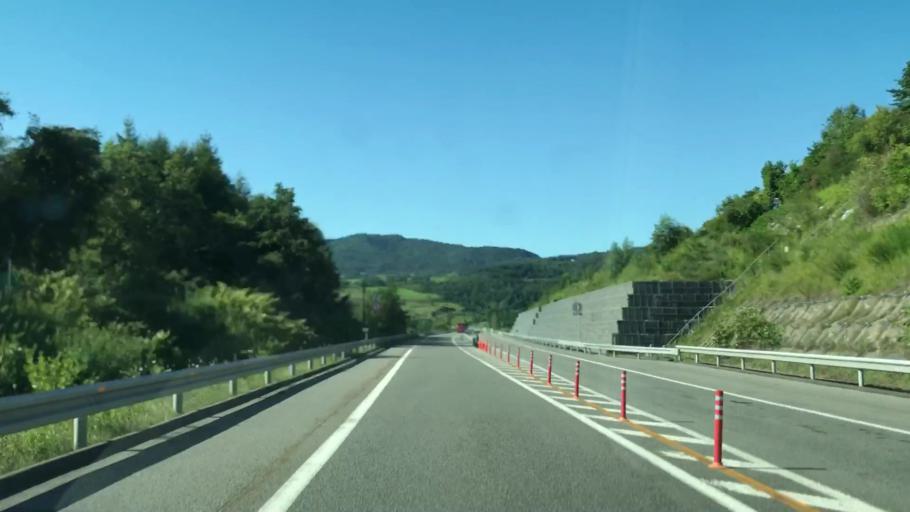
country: JP
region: Hokkaido
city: Date
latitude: 42.5413
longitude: 140.7949
